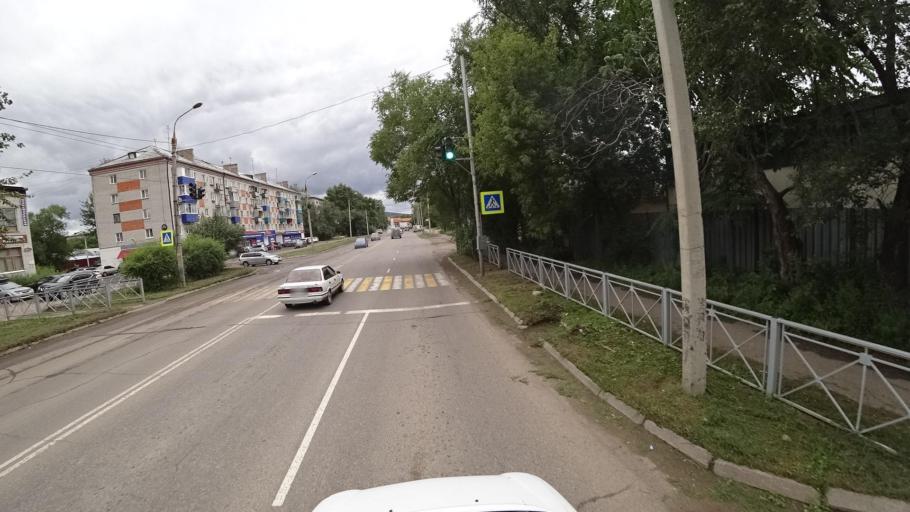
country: RU
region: Khabarovsk Krai
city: Komsomolsk-on-Amur
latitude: 50.5611
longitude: 137.0204
